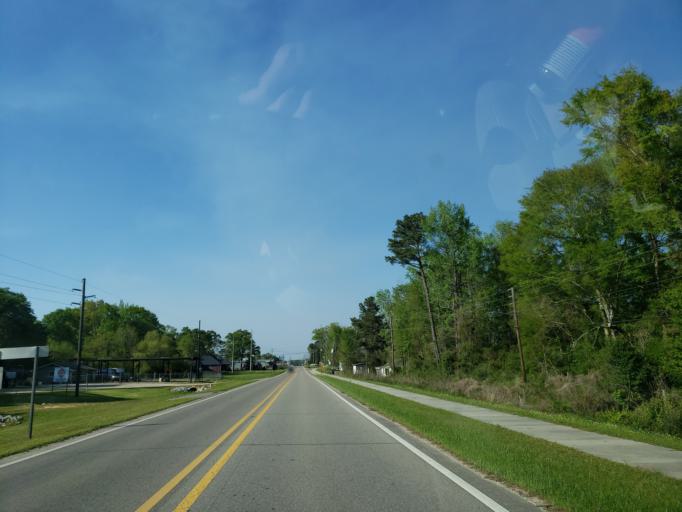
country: US
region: Mississippi
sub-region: Perry County
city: Richton
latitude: 31.3412
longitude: -88.9365
